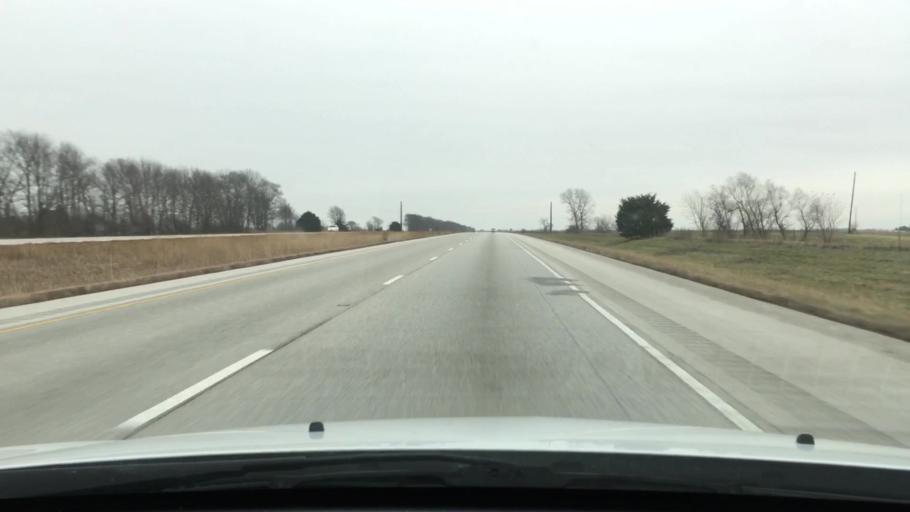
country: US
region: Illinois
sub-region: Scott County
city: Winchester
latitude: 39.6801
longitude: -90.3810
